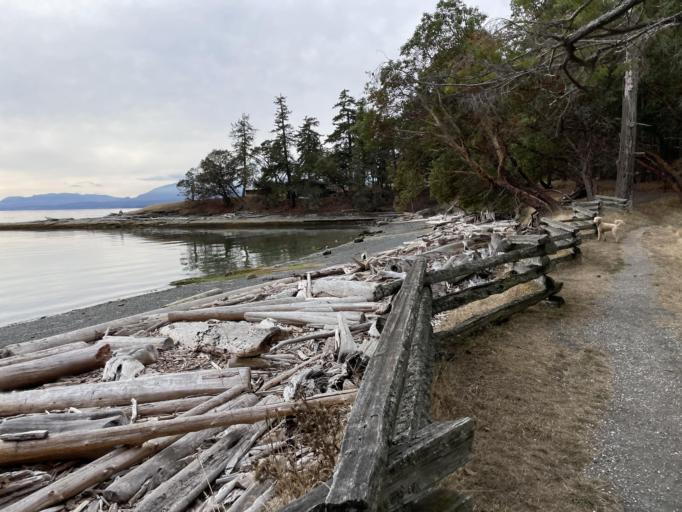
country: CA
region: British Columbia
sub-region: Cowichan Valley Regional District
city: Ladysmith
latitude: 49.0943
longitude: -123.7256
